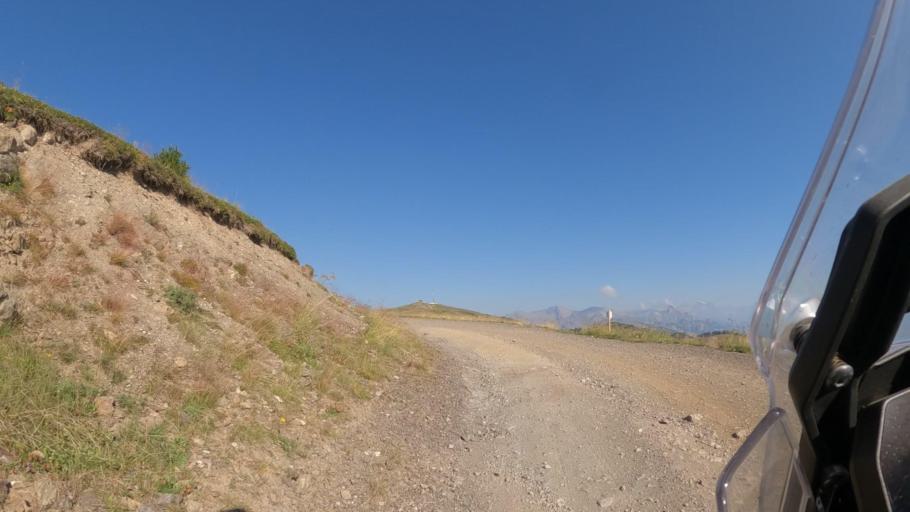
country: FR
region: Provence-Alpes-Cote d'Azur
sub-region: Departement des Hautes-Alpes
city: Guillestre
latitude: 44.6056
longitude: 6.6275
